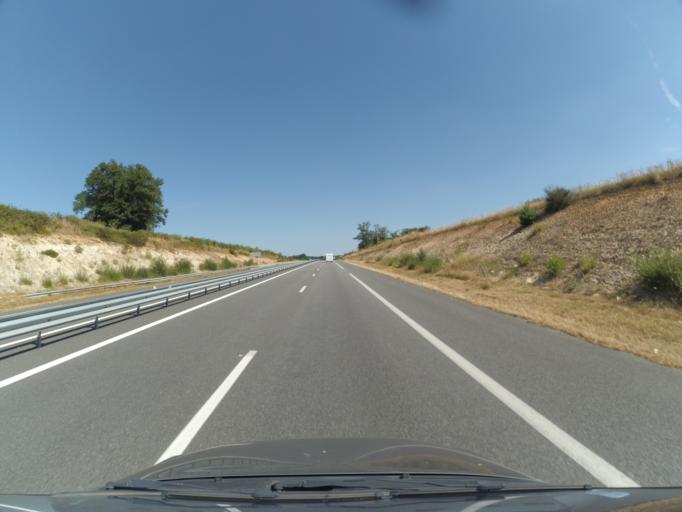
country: FR
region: Limousin
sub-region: Departement de la Haute-Vienne
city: Veyrac
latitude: 45.8863
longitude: 1.0764
